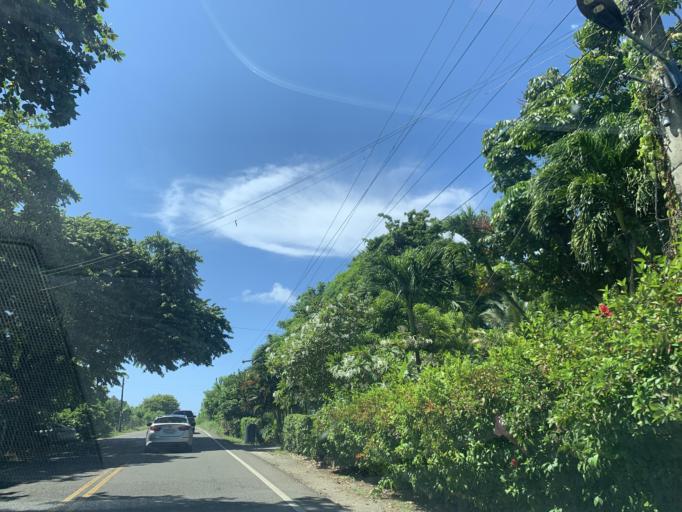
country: DO
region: Maria Trinidad Sanchez
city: Cabrera
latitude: 19.6644
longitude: -69.9434
